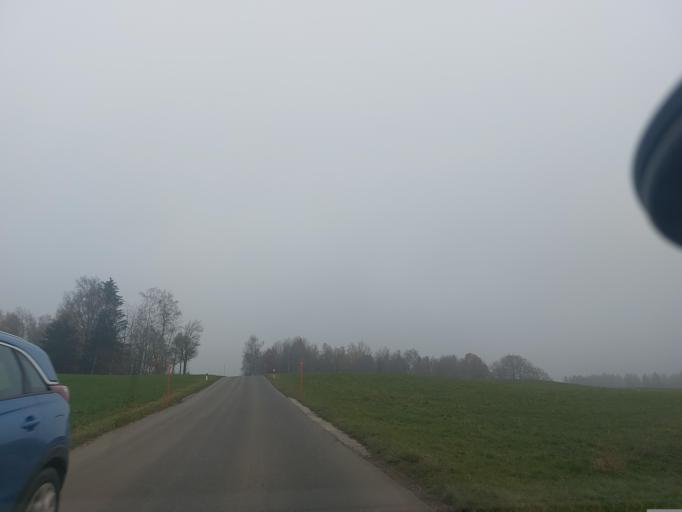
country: CH
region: Fribourg
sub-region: Veveyse District
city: Chatel-Saint-Denis
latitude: 46.5665
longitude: 6.8982
